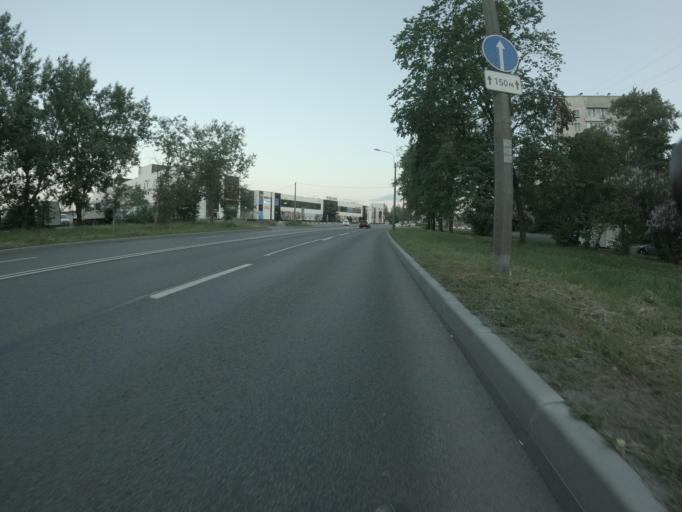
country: RU
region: St.-Petersburg
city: Dachnoye
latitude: 59.8459
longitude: 30.2800
